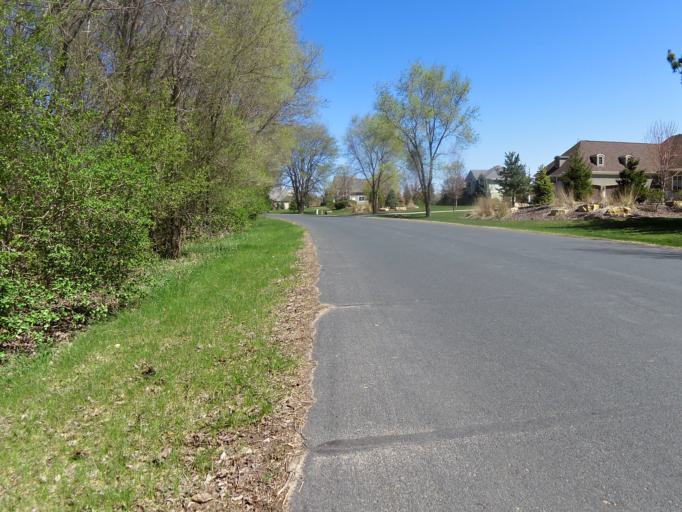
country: US
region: Minnesota
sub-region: Washington County
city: Lakeland
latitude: 44.9551
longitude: -92.8294
